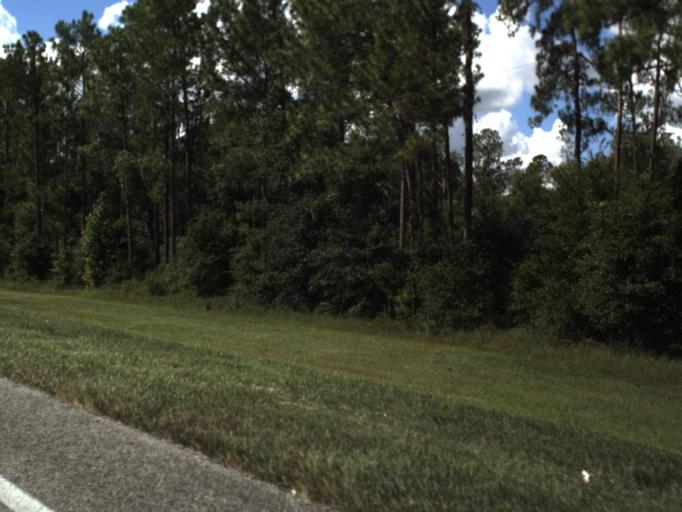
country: US
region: Florida
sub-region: Pasco County
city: Zephyrhills North
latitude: 28.2990
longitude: -82.0558
